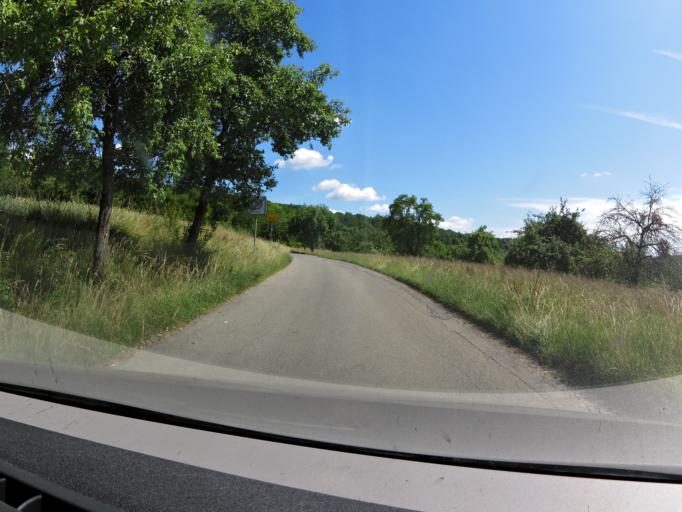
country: DE
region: Baden-Wuerttemberg
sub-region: Tuebingen Region
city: Tuebingen
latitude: 48.5450
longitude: 9.0112
